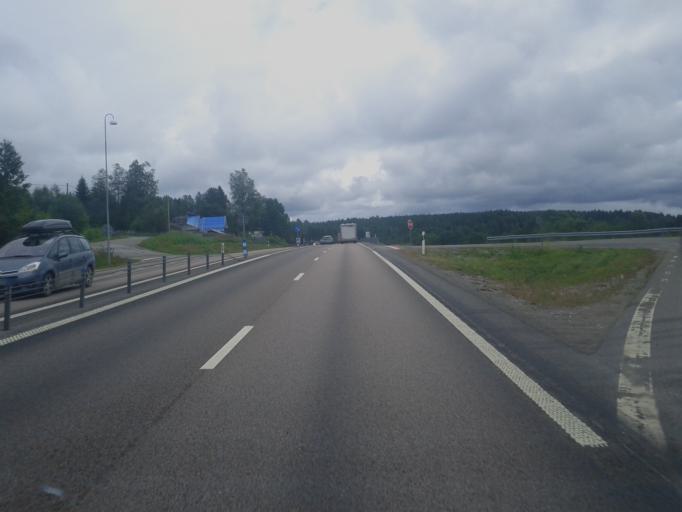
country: SE
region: Vaesternorrland
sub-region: Timra Kommun
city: Soraker
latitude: 62.5580
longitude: 17.6607
